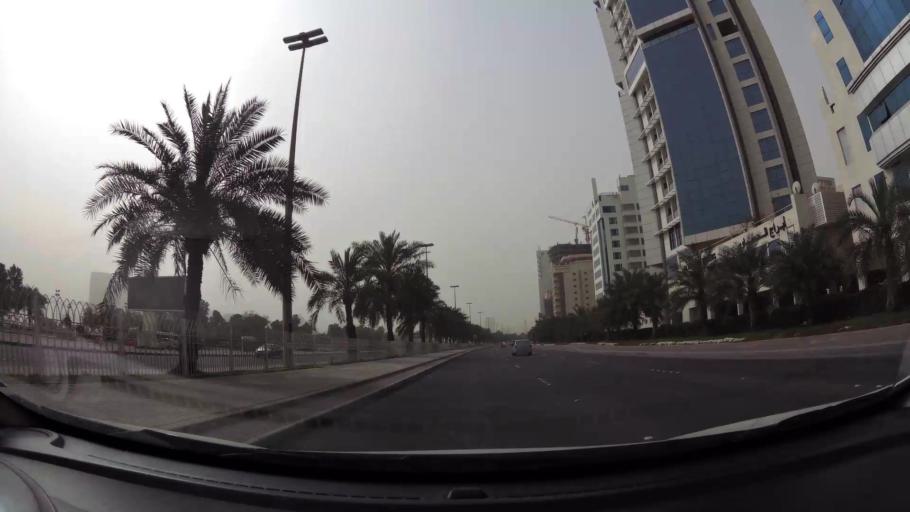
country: BH
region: Manama
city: Manama
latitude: 26.2307
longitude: 50.5987
